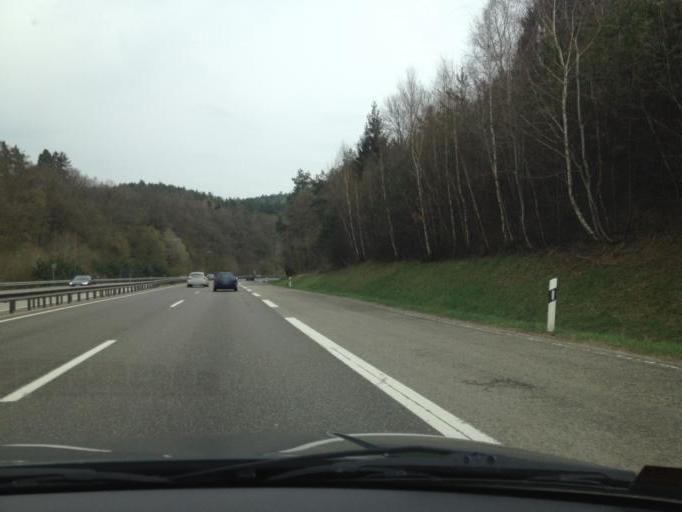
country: DE
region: Rheinland-Pfalz
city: Rodalben
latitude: 49.2143
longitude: 7.6484
